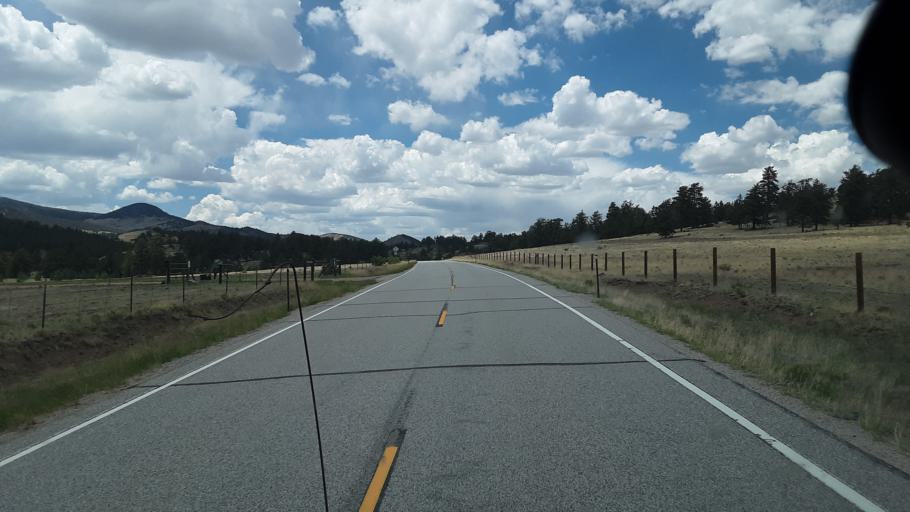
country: US
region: Colorado
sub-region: Teller County
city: Cripple Creek
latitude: 38.7808
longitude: -105.5709
